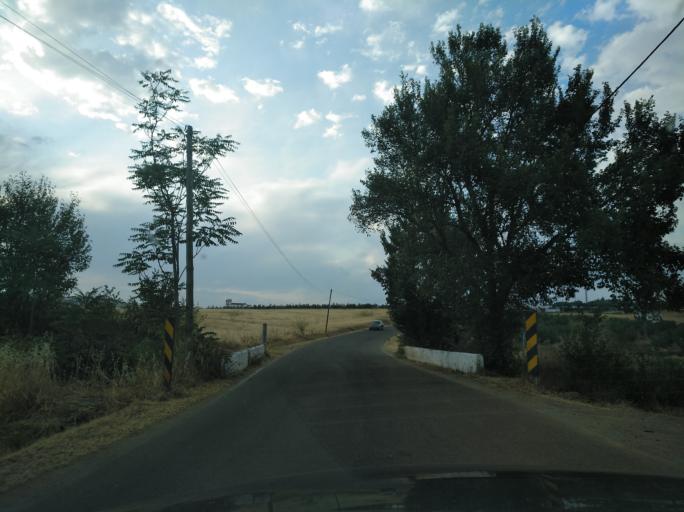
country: PT
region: Portalegre
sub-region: Campo Maior
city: Campo Maior
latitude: 39.0061
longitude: -7.0607
